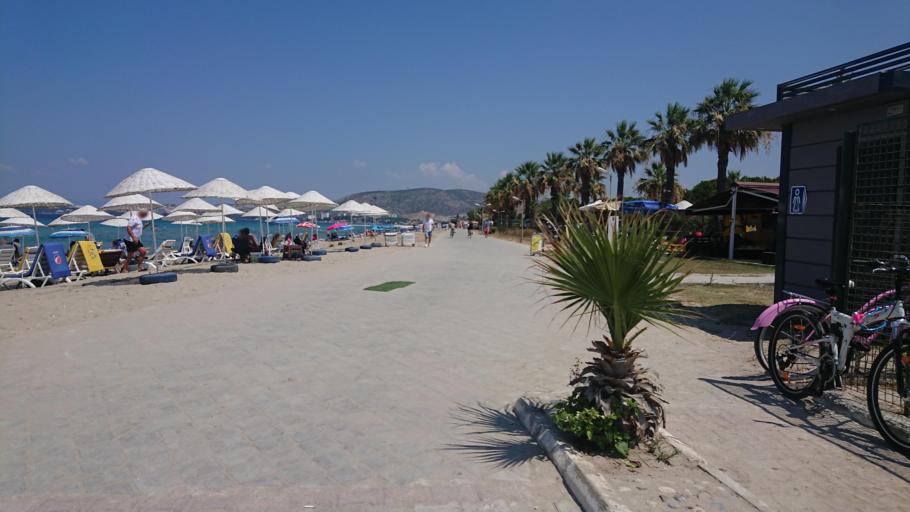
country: TR
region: Aydin
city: Kusadasi
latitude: 37.7957
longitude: 27.2683
